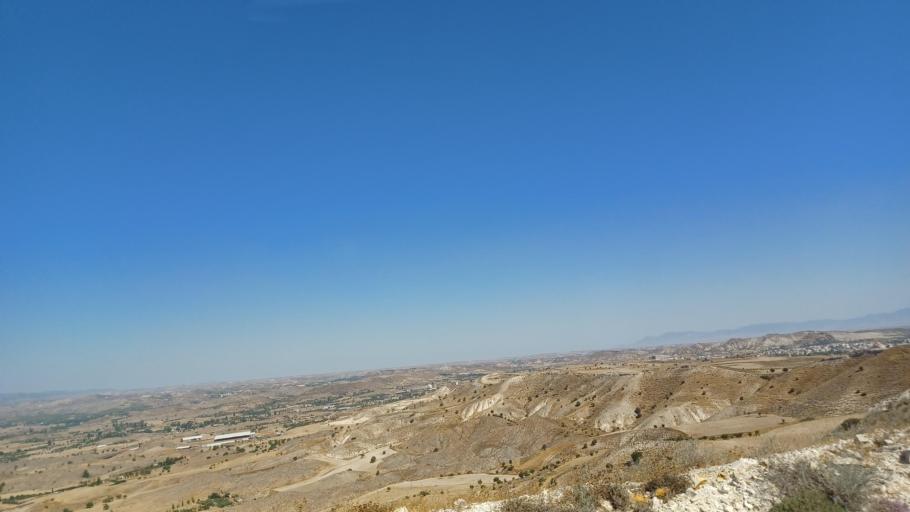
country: CY
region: Larnaka
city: Psevdas
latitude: 34.9687
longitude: 33.4788
